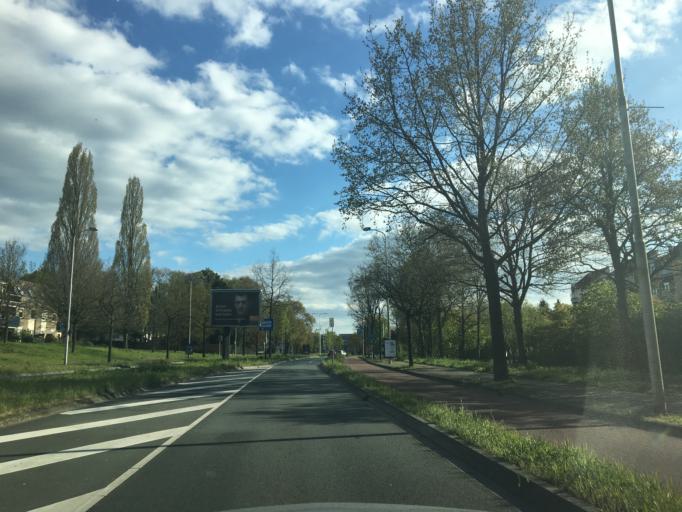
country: NL
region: Gelderland
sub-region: Gemeente Ede
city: Ede
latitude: 52.0487
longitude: 5.6752
